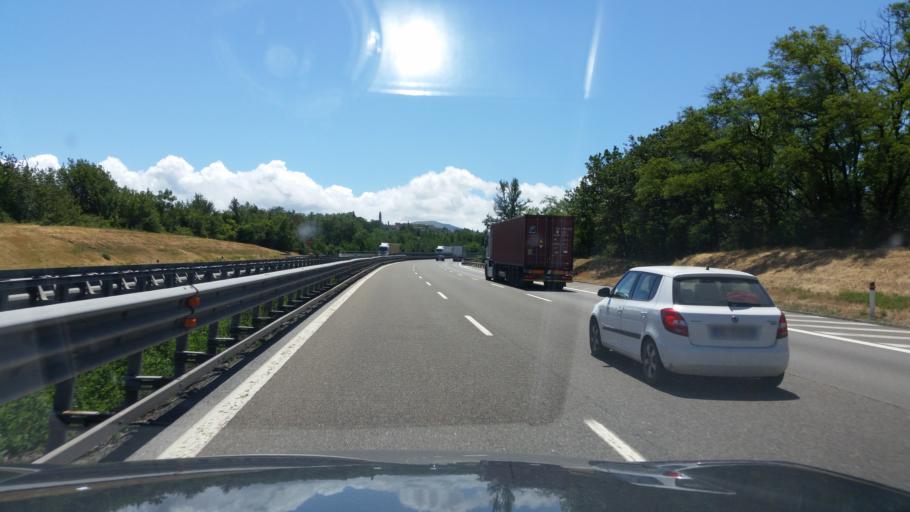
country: IT
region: Piedmont
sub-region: Provincia di Alessandria
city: Tagliolo Monferrato
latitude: 44.6519
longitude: 8.6607
